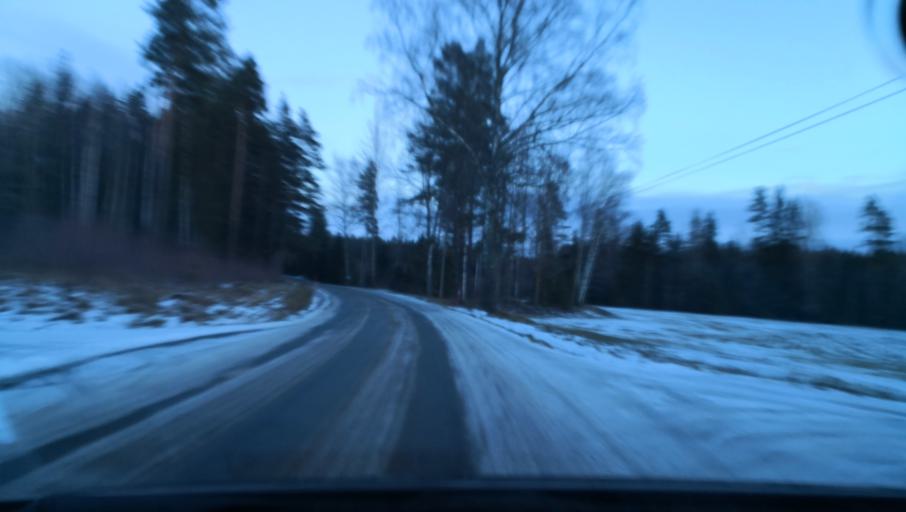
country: SE
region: Soedermanland
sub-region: Katrineholms Kommun
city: Katrineholm
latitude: 59.0806
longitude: 16.2365
